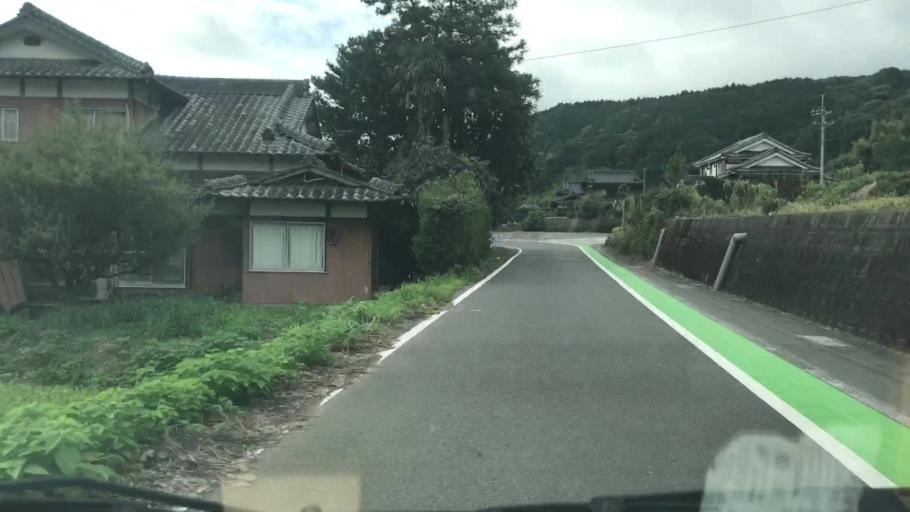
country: JP
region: Saga Prefecture
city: Takeocho-takeo
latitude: 33.2232
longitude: 130.0240
